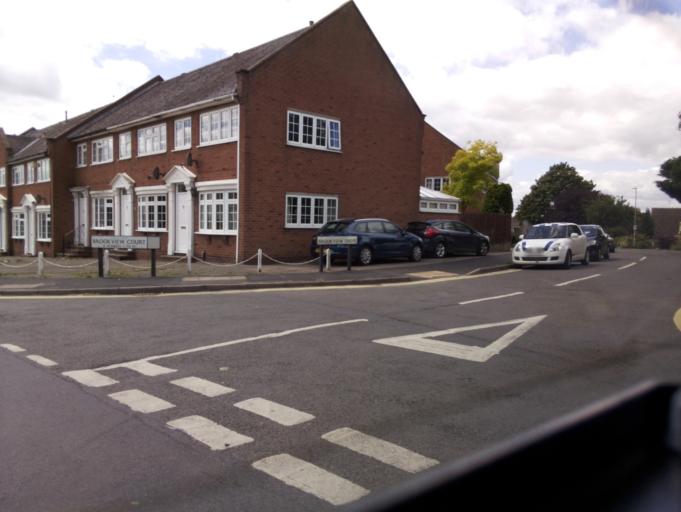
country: GB
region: England
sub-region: Nottinghamshire
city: Ruddington
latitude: 52.8695
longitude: -1.0898
